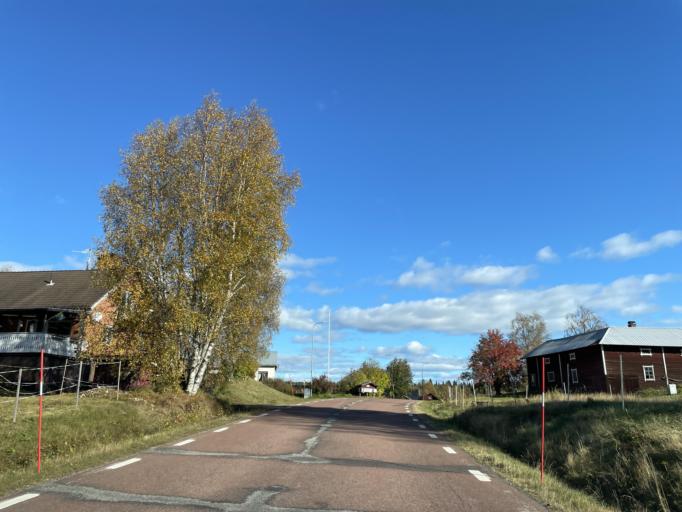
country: SE
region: Dalarna
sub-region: Malung-Saelens kommun
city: Malung
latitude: 60.8440
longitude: 13.4081
